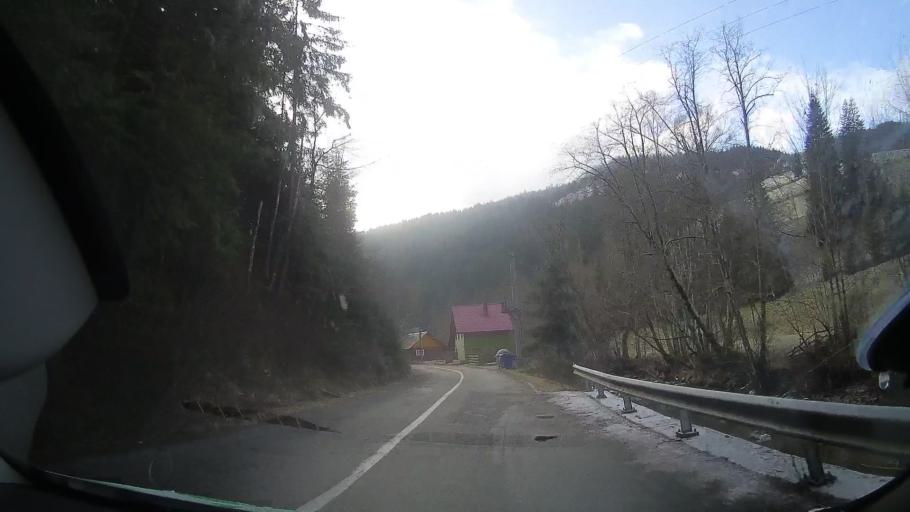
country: RO
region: Alba
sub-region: Comuna Horea
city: Horea
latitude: 46.4784
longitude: 22.9609
